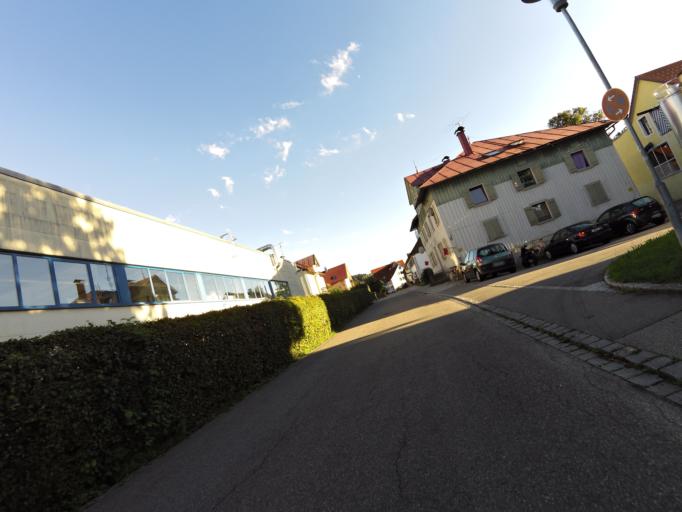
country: DE
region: Bavaria
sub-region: Swabia
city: Weiler-Simmerberg
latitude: 47.5841
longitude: 9.9148
